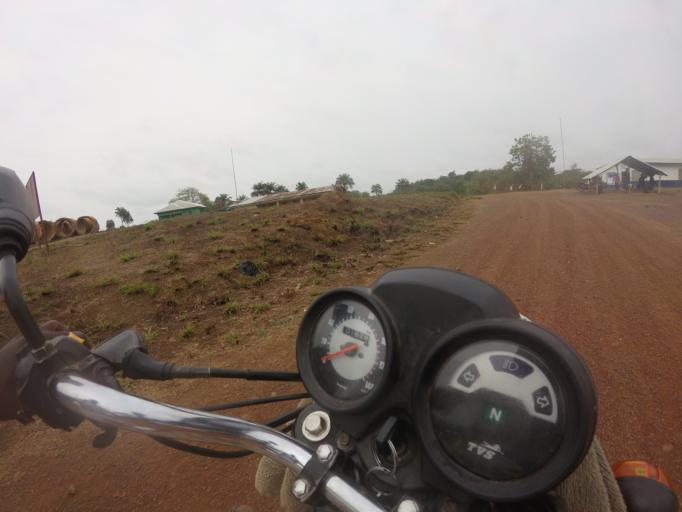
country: SL
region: Southern Province
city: Zimmi
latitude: 7.2178
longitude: -11.1796
